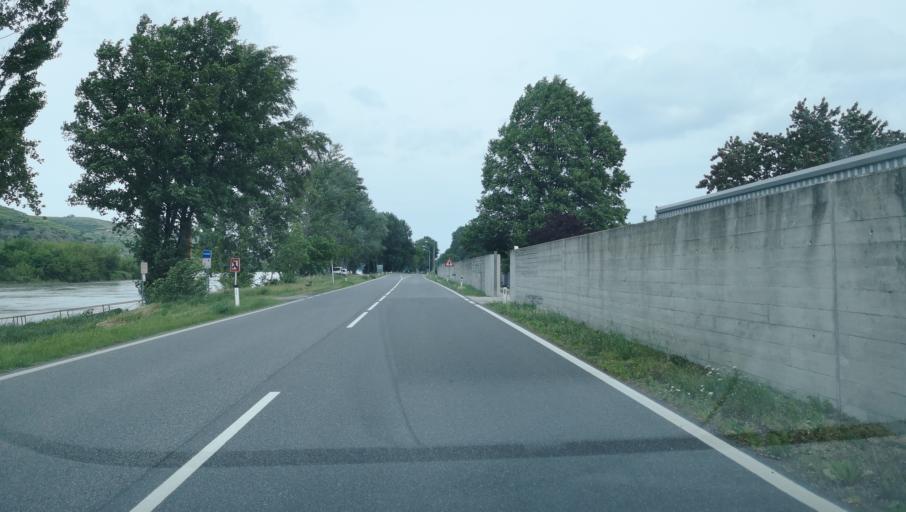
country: AT
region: Lower Austria
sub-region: Politischer Bezirk Krems
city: Durnstein
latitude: 48.3886
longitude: 15.5586
